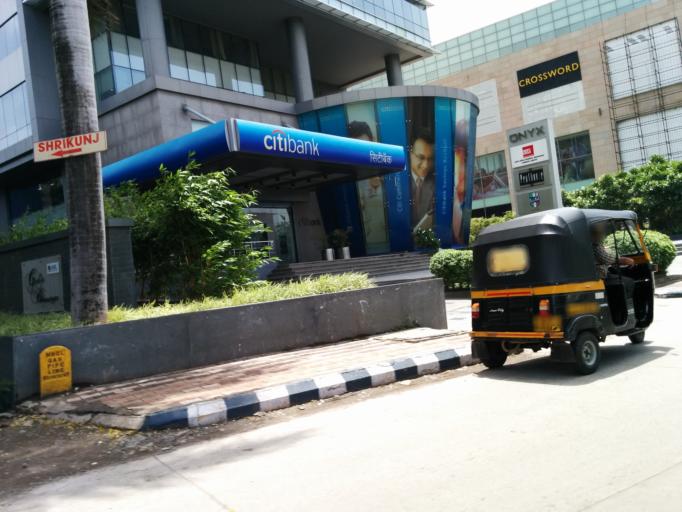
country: IN
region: Maharashtra
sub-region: Pune Division
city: Pune
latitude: 18.5382
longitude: 73.9067
